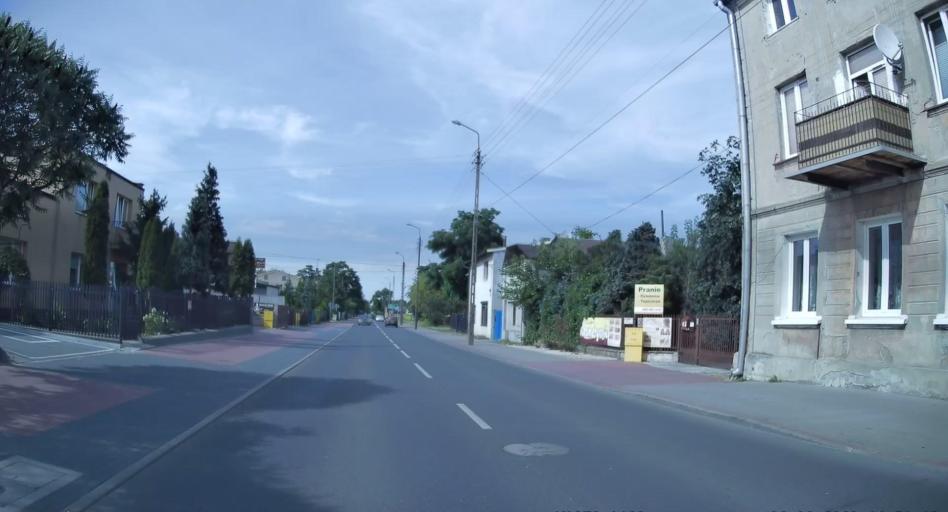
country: PL
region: Lodz Voivodeship
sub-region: Powiat tomaszowski
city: Tomaszow Mazowiecki
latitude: 51.5287
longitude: 19.9971
